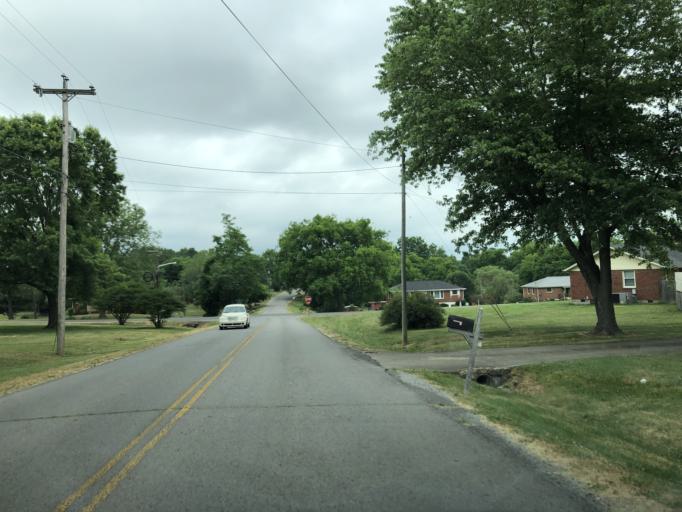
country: US
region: Tennessee
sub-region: Davidson County
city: Goodlettsville
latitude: 36.2825
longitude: -86.7267
